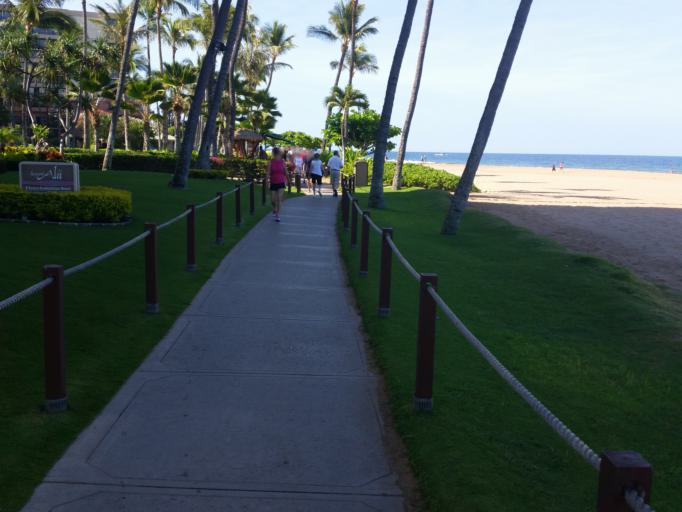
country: US
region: Hawaii
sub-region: Maui County
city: Ka'anapali
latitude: 20.9179
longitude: -156.6964
